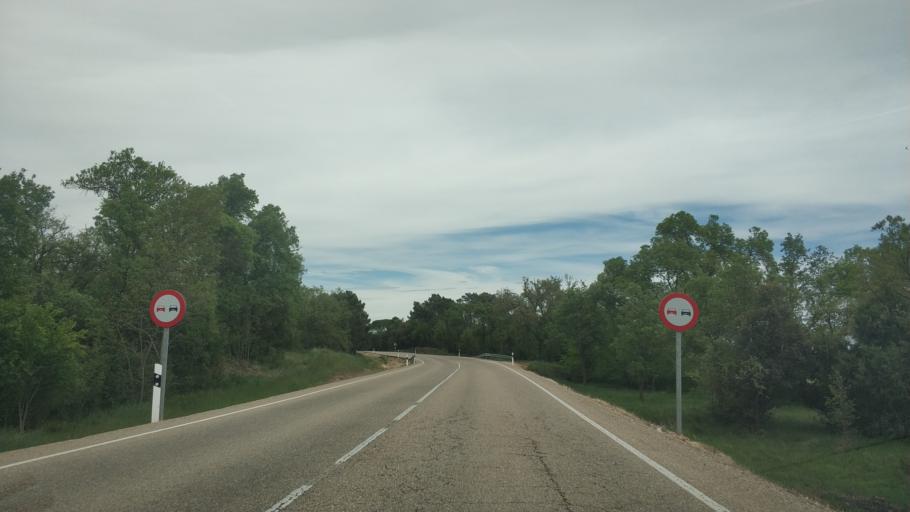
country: ES
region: Castille and Leon
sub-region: Provincia de Soria
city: Bayubas de Abajo
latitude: 41.5053
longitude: -2.9006
